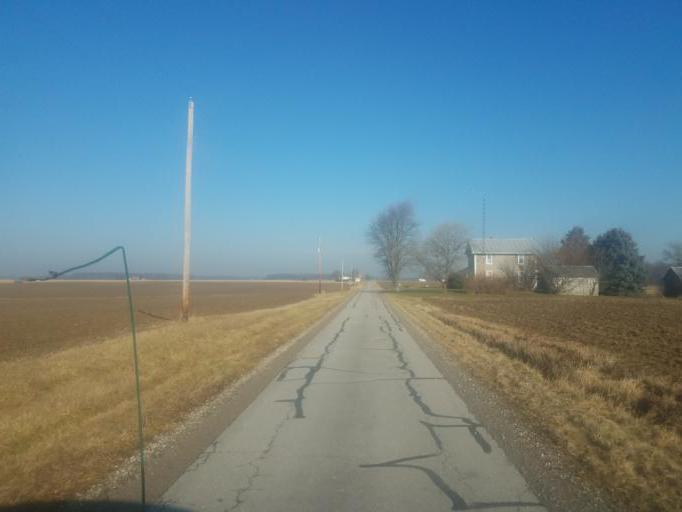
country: US
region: Ohio
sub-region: Huron County
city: Willard
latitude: 41.0239
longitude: -82.9390
